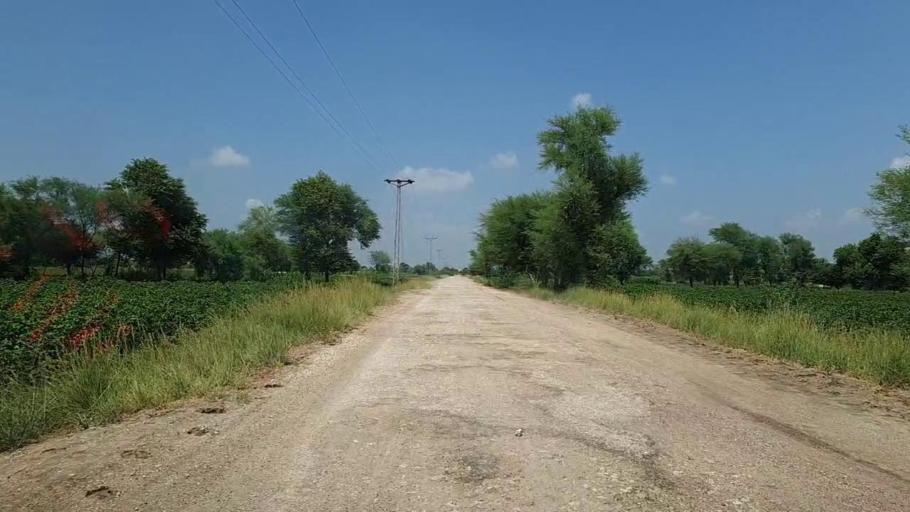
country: PK
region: Sindh
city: Kandiaro
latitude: 26.9932
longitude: 68.2503
